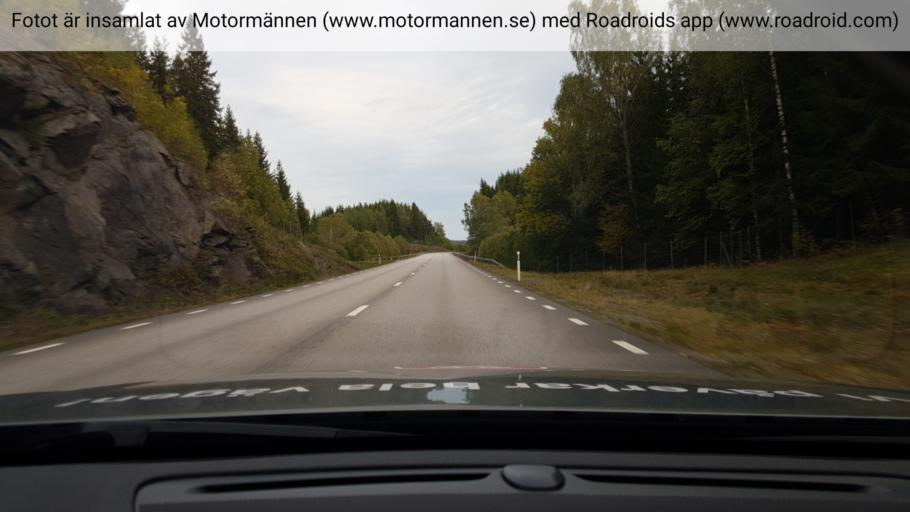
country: SE
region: Vaestra Goetaland
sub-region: Bengtsfors Kommun
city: Billingsfors
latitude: 59.0279
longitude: 12.3483
